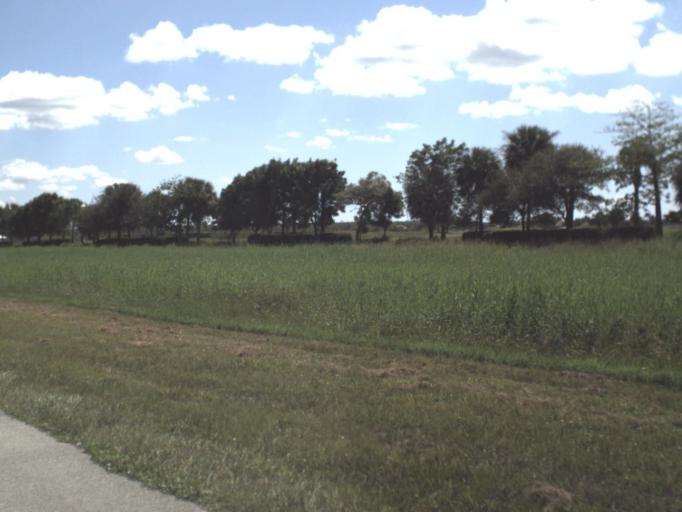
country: US
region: Florida
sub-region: Collier County
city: Lely Resort
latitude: 26.0164
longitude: -81.6259
